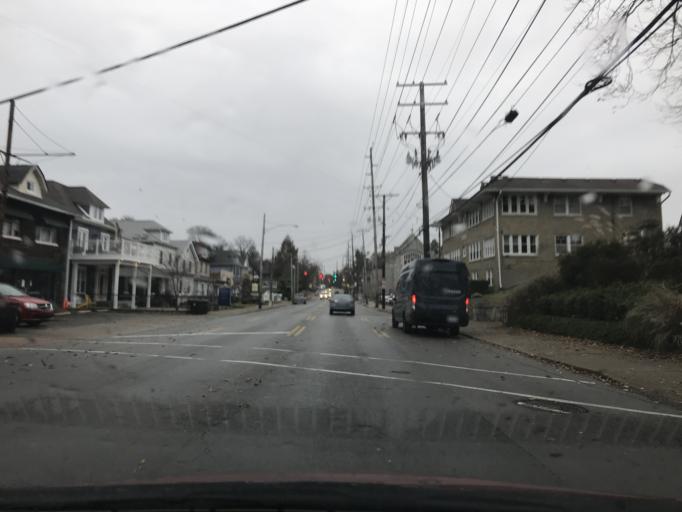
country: US
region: Kentucky
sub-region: Jefferson County
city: Audubon Park
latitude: 38.2285
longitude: -85.7012
